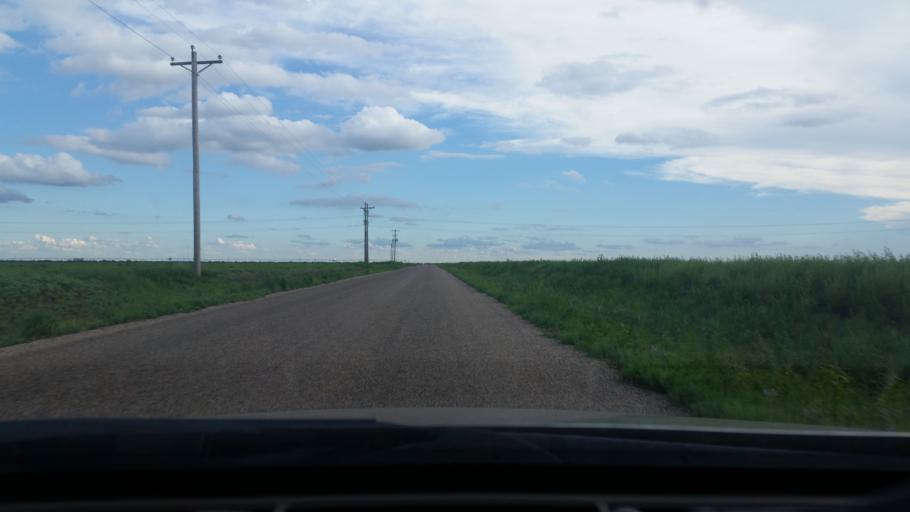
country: US
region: New Mexico
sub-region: Curry County
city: Clovis
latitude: 34.4577
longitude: -103.2316
